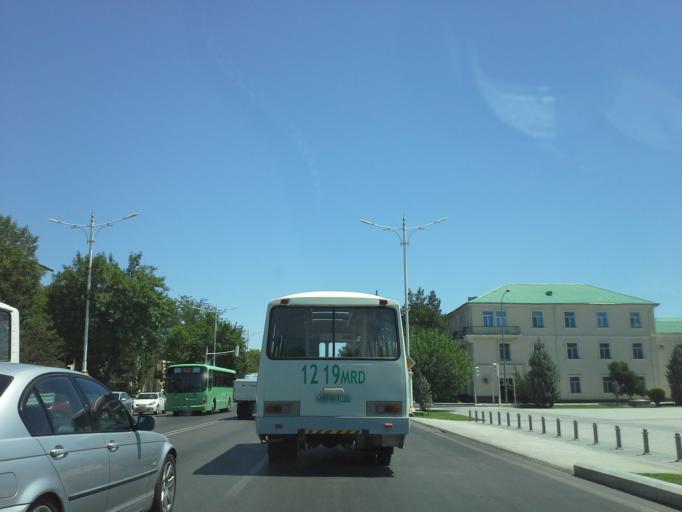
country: TM
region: Ahal
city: Ashgabat
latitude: 37.9499
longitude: 58.3733
